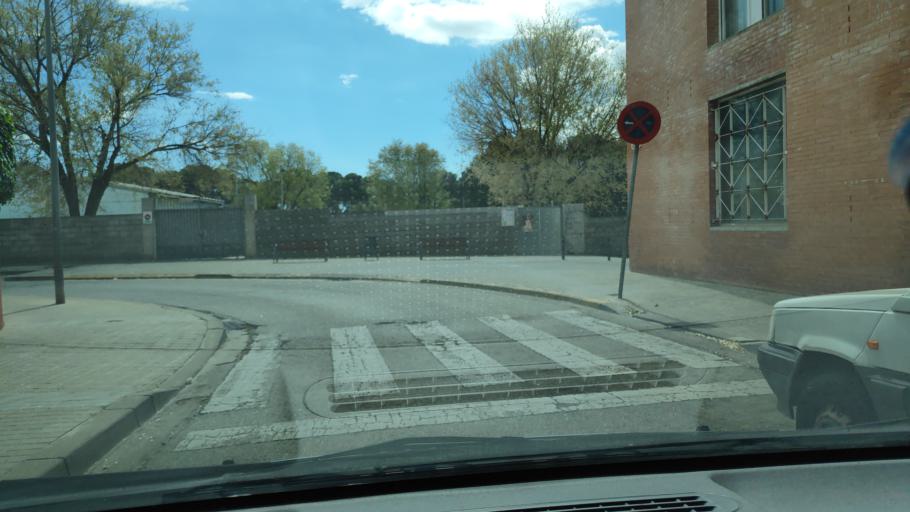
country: ES
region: Catalonia
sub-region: Provincia de Barcelona
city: Sabadell
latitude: 41.5402
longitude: 2.1300
